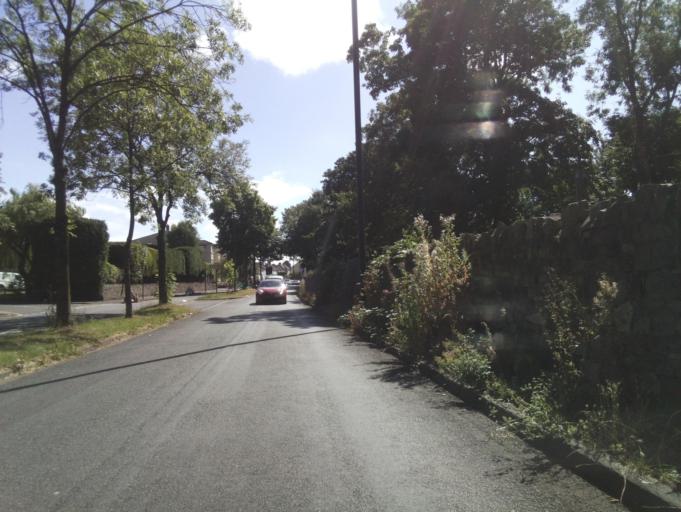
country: GB
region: England
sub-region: Bristol
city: Bristol
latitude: 51.4913
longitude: -2.6076
